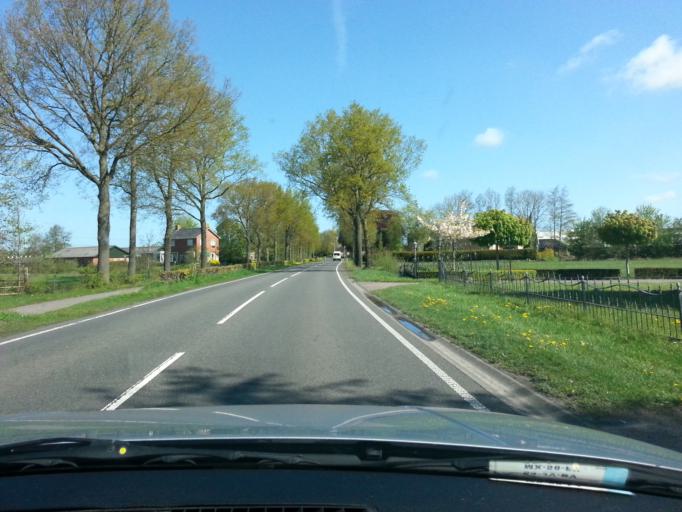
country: NL
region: Friesland
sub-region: Gemeente Achtkarspelen
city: Surhuizum
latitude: 53.1899
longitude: 6.1854
